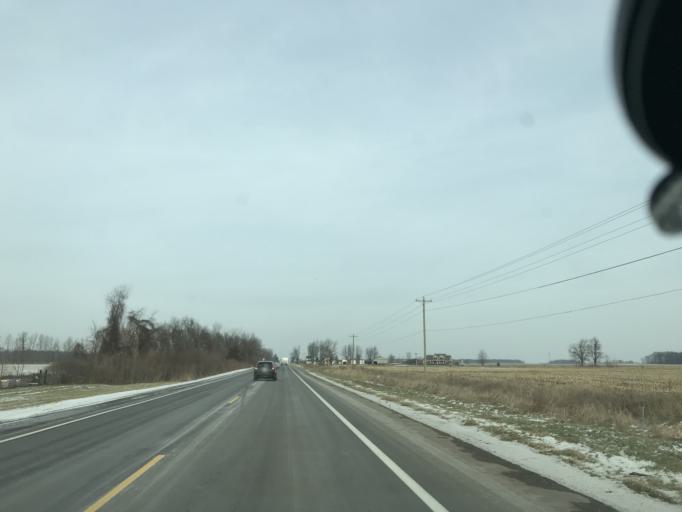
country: US
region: Michigan
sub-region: Ionia County
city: Lake Odessa
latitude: 42.8111
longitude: -85.0746
